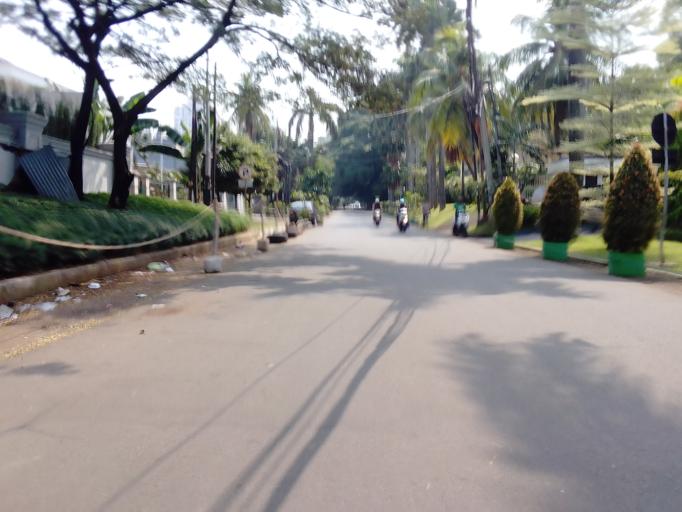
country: ID
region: Jakarta Raya
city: Jakarta
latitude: -6.2280
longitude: 106.7947
